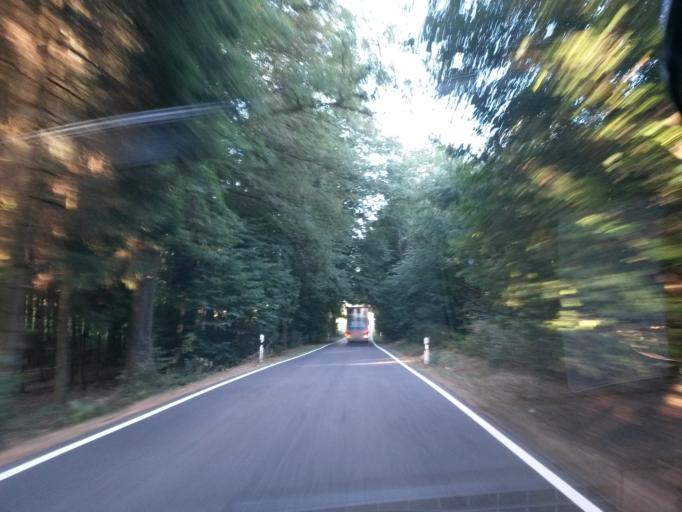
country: DE
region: North Rhine-Westphalia
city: Wipperfurth
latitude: 51.1036
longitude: 7.4645
